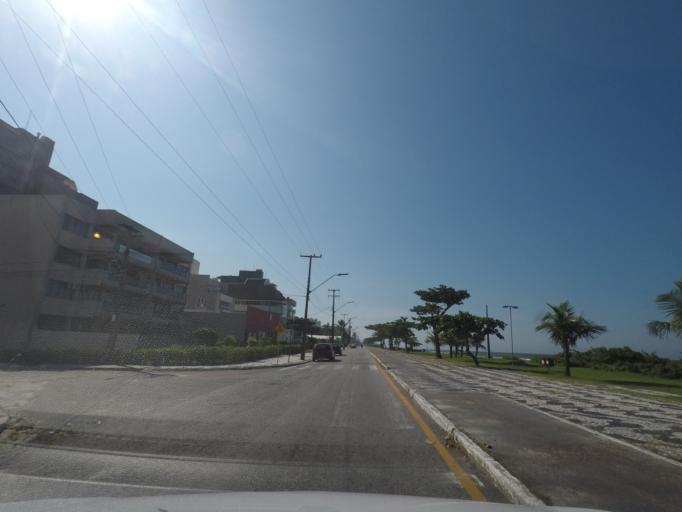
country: BR
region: Parana
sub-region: Guaratuba
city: Guaratuba
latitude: -25.8285
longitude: -48.5350
